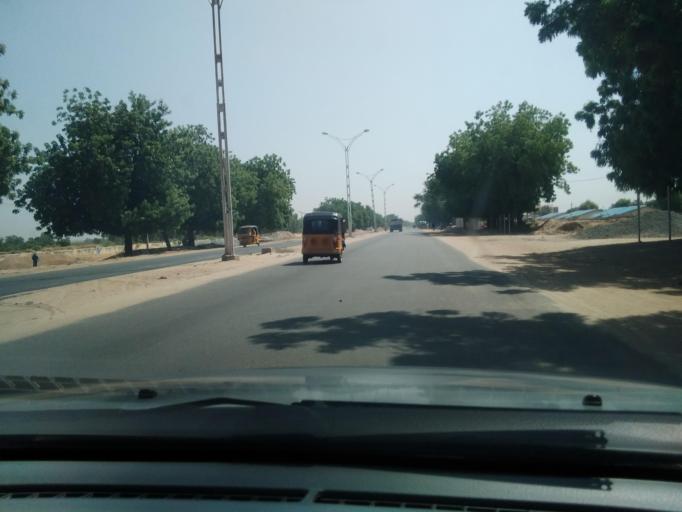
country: NG
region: Borno
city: Maiduguri
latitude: 11.7952
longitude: 13.1983
